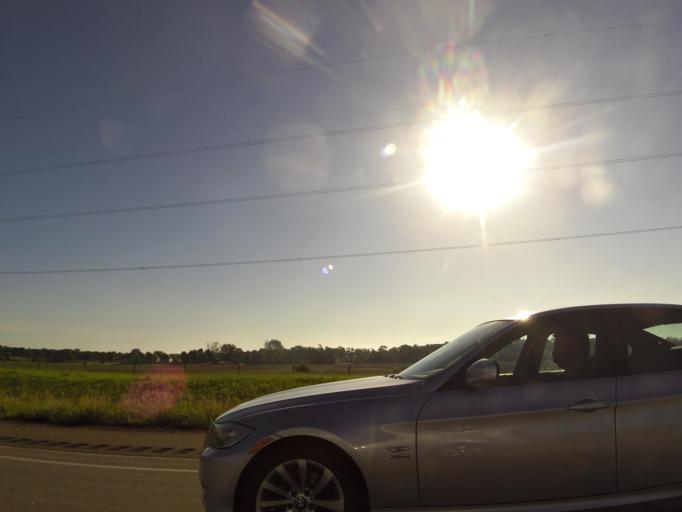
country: US
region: Minnesota
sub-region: Stearns County
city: Saint Augusta
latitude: 45.4536
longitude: -94.1227
